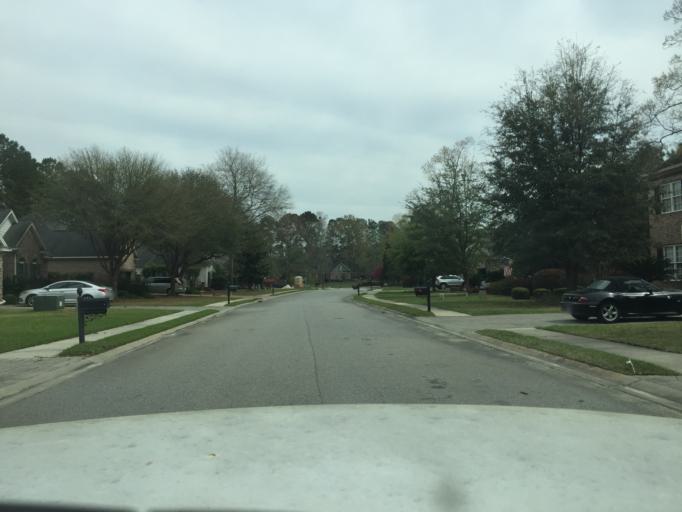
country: US
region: Georgia
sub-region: Chatham County
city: Pooler
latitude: 32.0661
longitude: -81.2463
